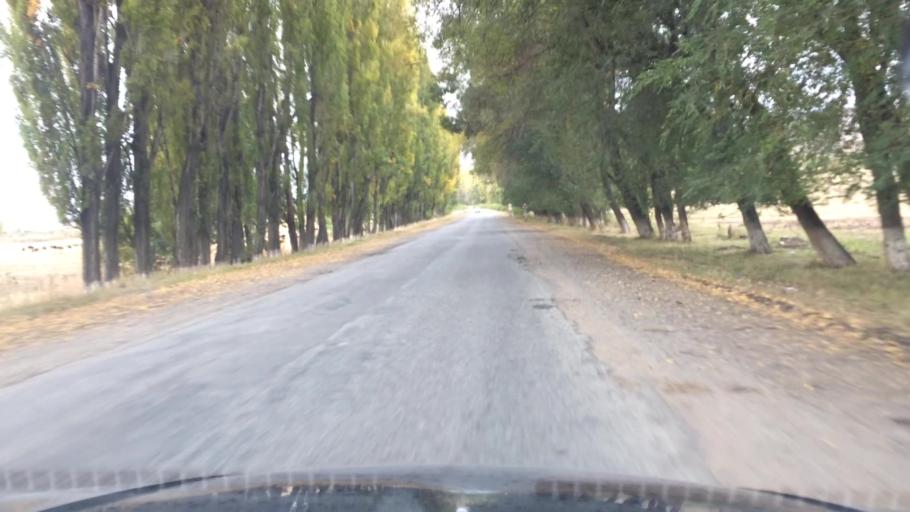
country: KG
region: Ysyk-Koel
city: Pokrovka
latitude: 42.7392
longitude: 77.9099
